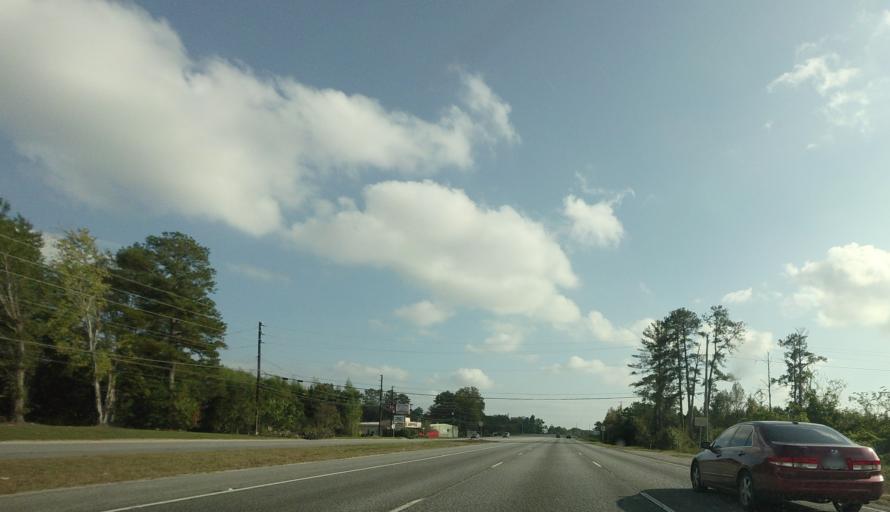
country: US
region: Georgia
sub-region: Bibb County
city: Macon
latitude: 32.7527
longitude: -83.6591
